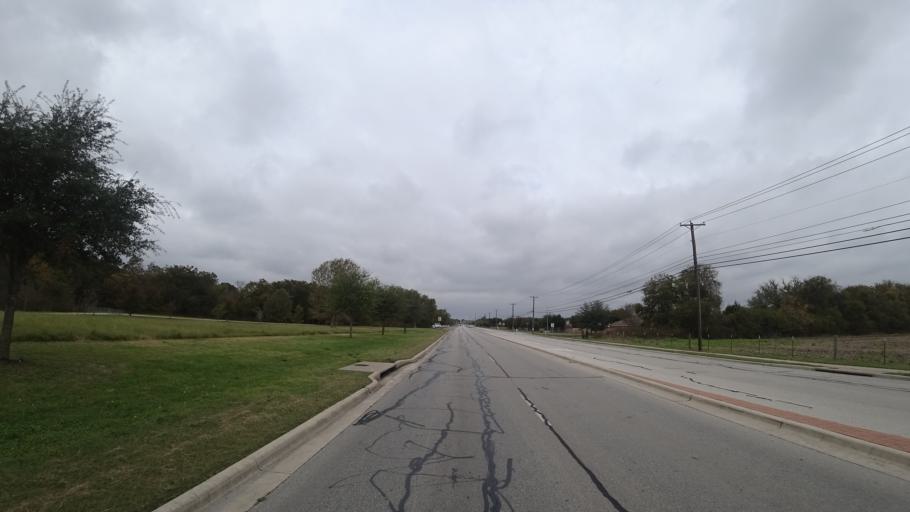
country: US
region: Texas
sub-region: Travis County
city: Pflugerville
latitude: 30.4321
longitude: -97.6046
